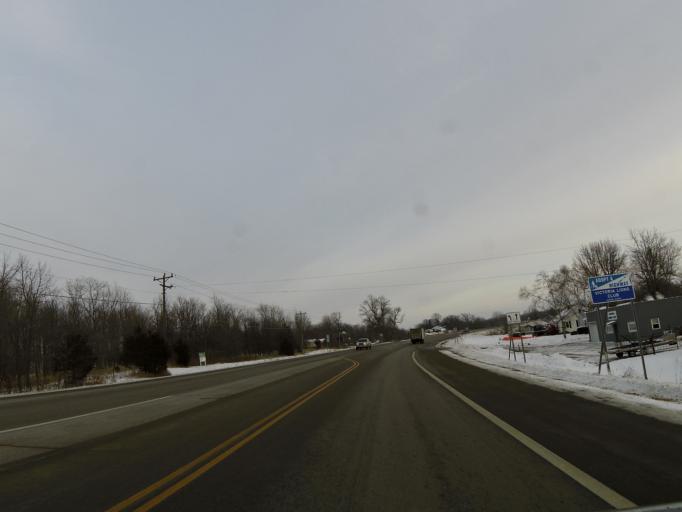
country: US
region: Minnesota
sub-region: Carver County
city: Victoria
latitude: 44.8615
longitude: -93.6709
